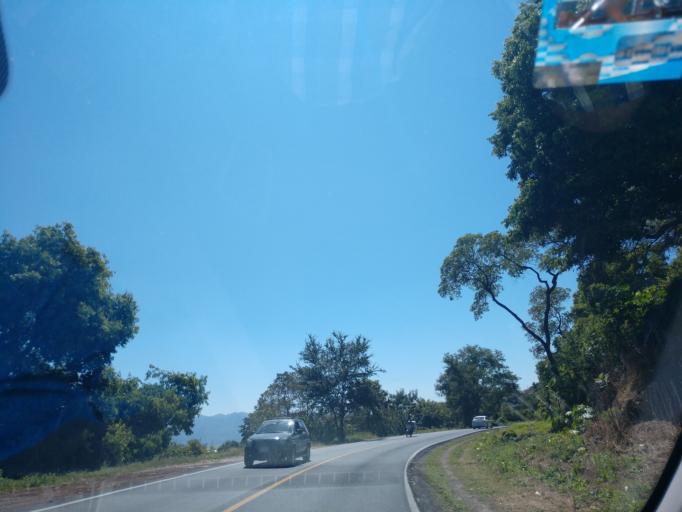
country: MX
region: Nayarit
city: Xalisco
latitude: 21.4074
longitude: -104.8961
